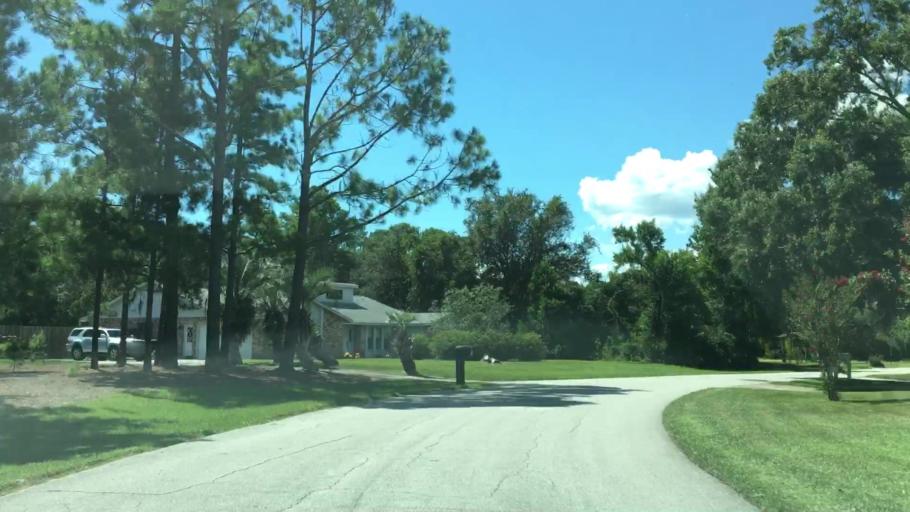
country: US
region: Florida
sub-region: Volusia County
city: Deltona
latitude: 28.8797
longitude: -81.2245
